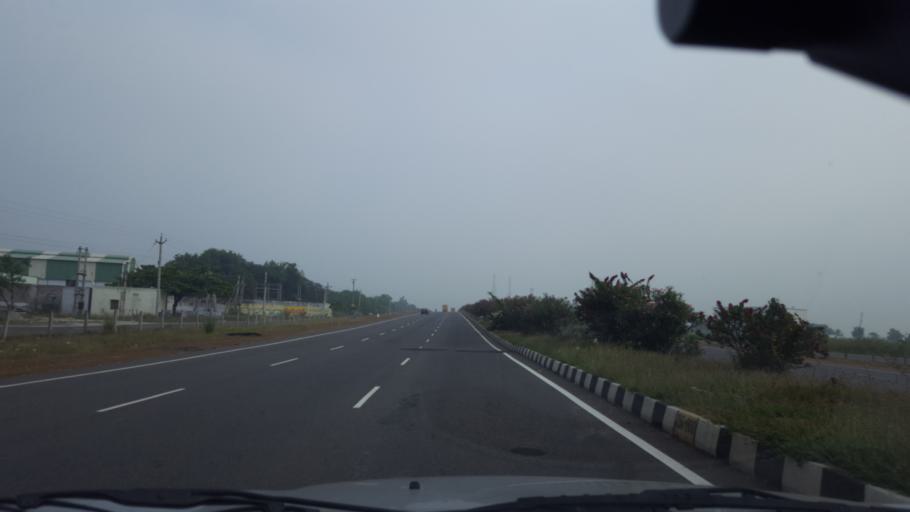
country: IN
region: Andhra Pradesh
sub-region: Guntur
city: Chilakalurupet
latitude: 16.0421
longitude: 80.1369
